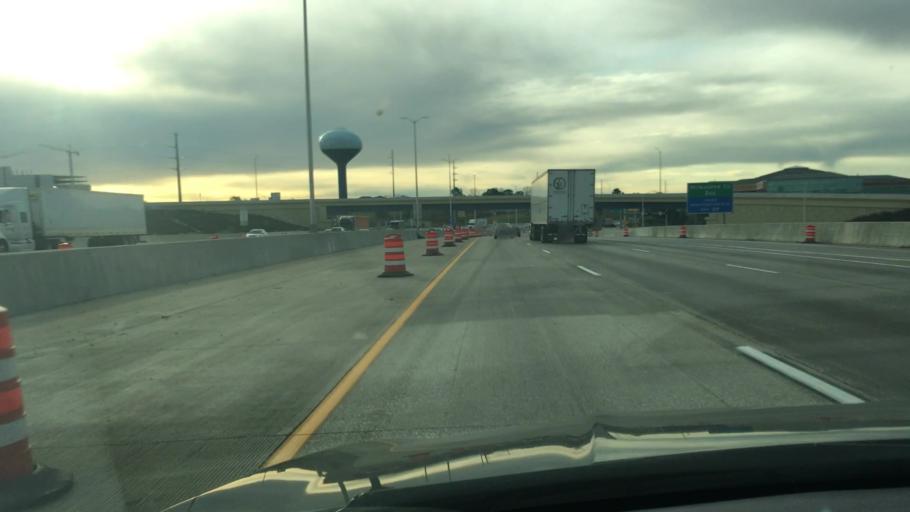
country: US
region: Wisconsin
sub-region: Milwaukee County
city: Wauwatosa
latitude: 43.0450
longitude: -88.0359
